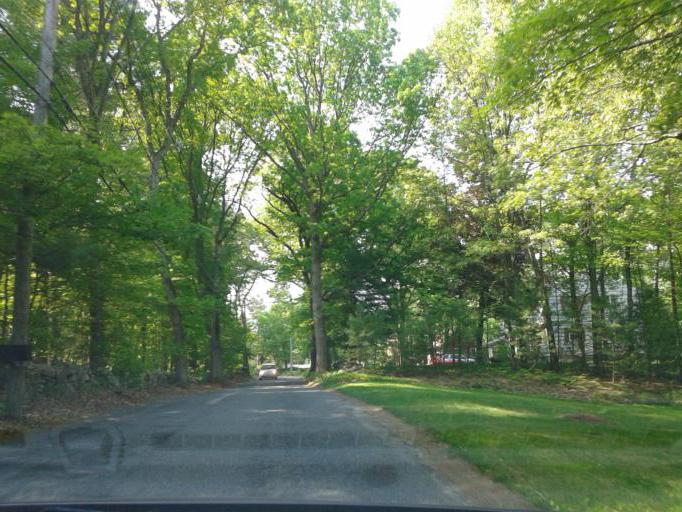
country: US
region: Massachusetts
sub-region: Worcester County
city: Westborough
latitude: 42.2398
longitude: -71.6121
